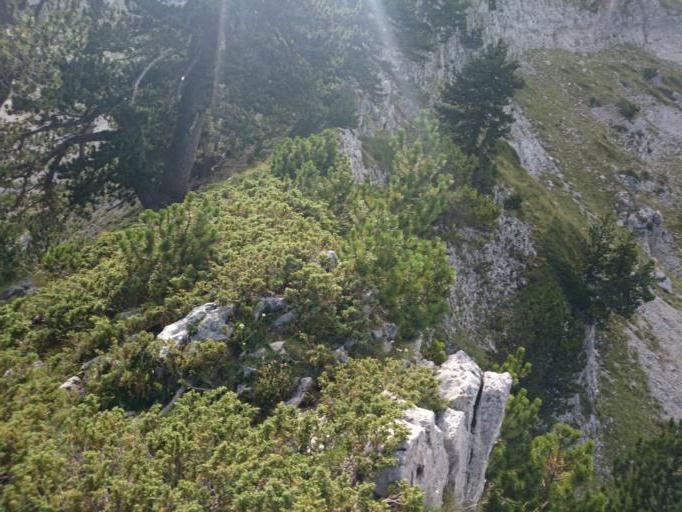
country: AL
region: Berat
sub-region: Rrethi i Beratit
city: Polican
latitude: 40.6500
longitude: 20.1605
